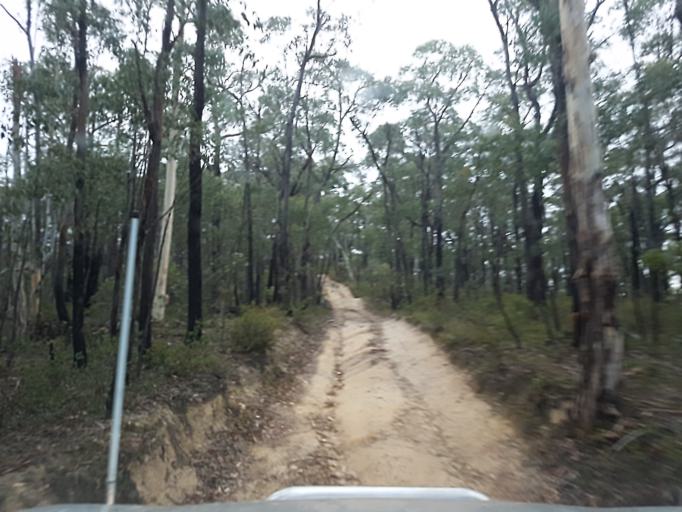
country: AU
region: New South Wales
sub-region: Snowy River
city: Jindabyne
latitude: -36.8540
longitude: 148.2297
